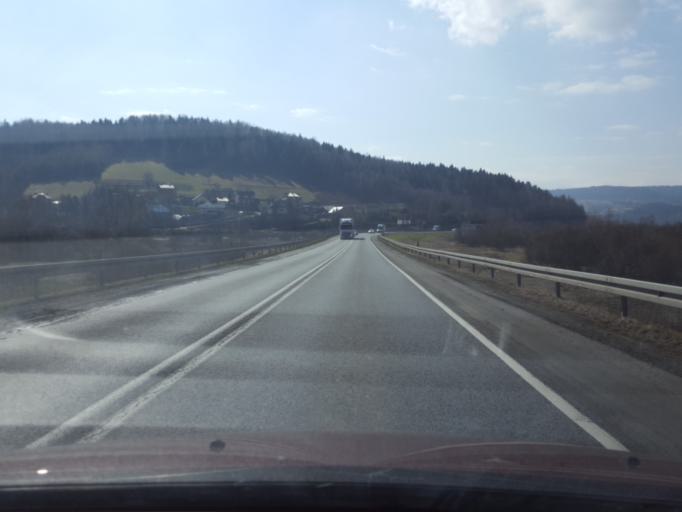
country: PL
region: Lesser Poland Voivodeship
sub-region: Powiat nowosadecki
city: Chelmiec
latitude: 49.6869
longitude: 20.6552
